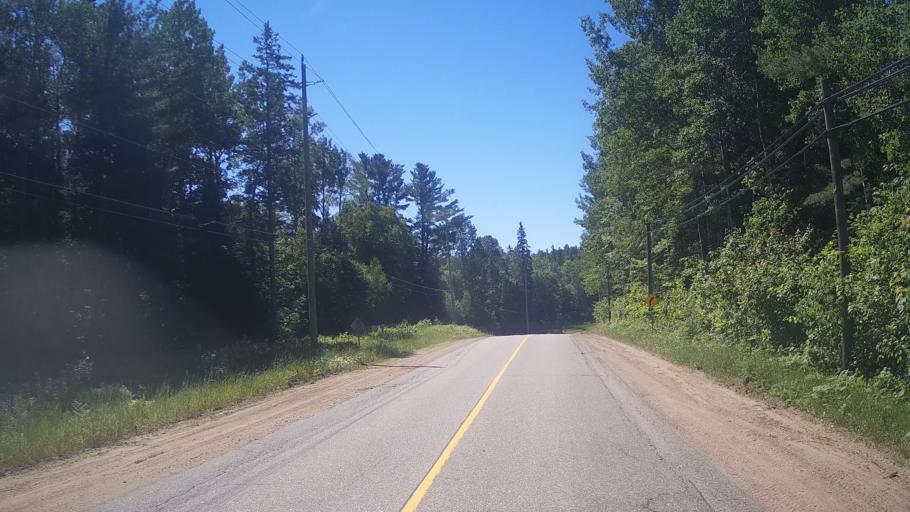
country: CA
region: Ontario
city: Huntsville
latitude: 45.3698
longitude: -79.2059
